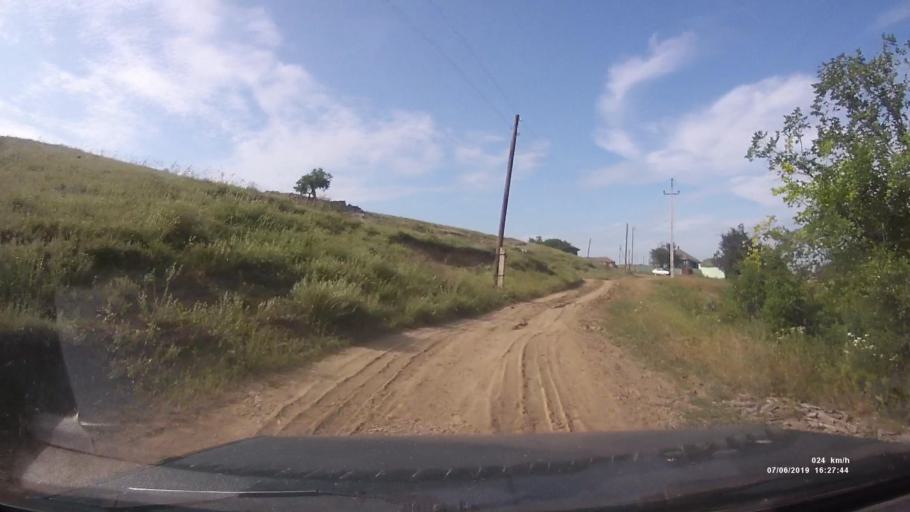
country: RU
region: Rostov
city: Staraya Stanitsa
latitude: 48.2534
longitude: 40.3185
